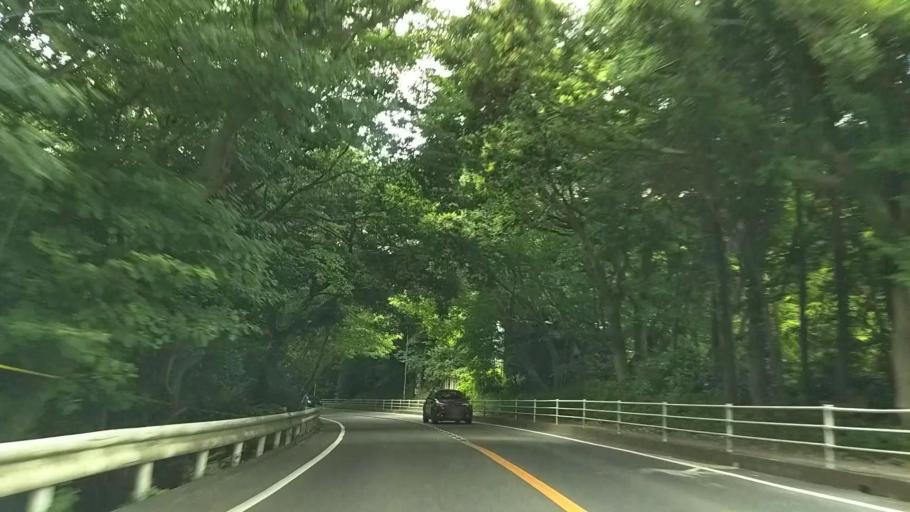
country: JP
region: Kanagawa
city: Chigasaki
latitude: 35.3677
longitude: 139.4117
